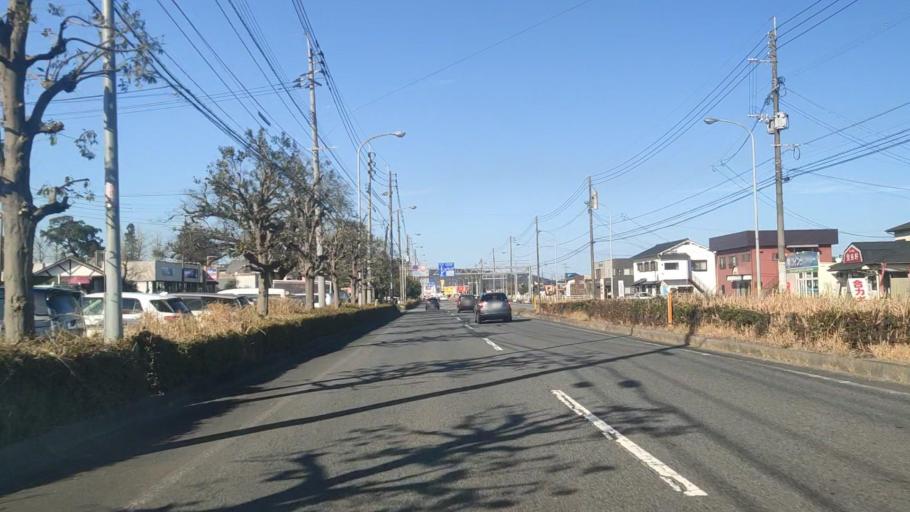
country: JP
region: Oita
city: Oita
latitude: 33.1449
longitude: 131.6578
